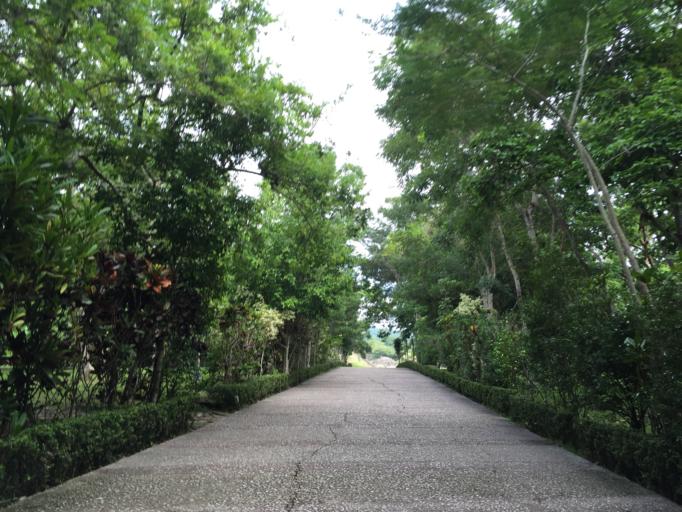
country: MX
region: Veracruz
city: Papantla de Olarte
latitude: 20.4434
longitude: -97.3778
